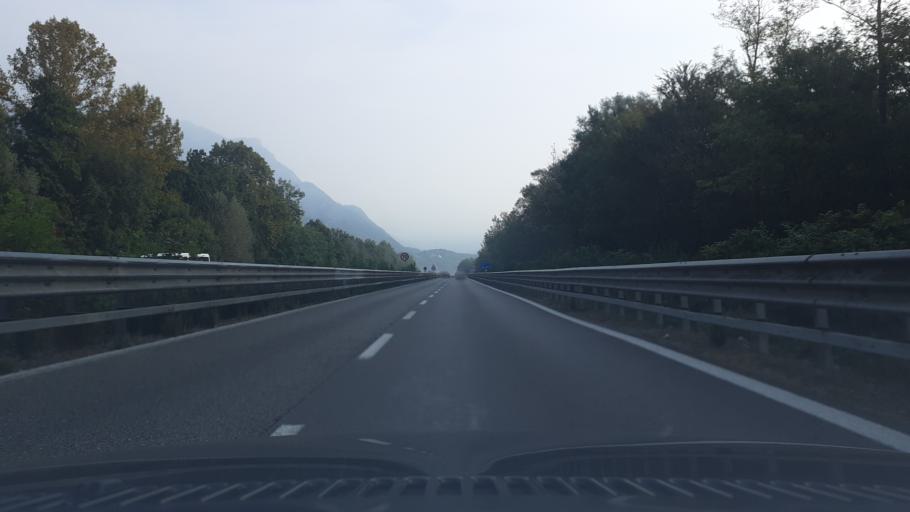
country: IT
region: Lombardy
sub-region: Provincia di Lecco
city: Suello
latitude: 45.8040
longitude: 9.3107
